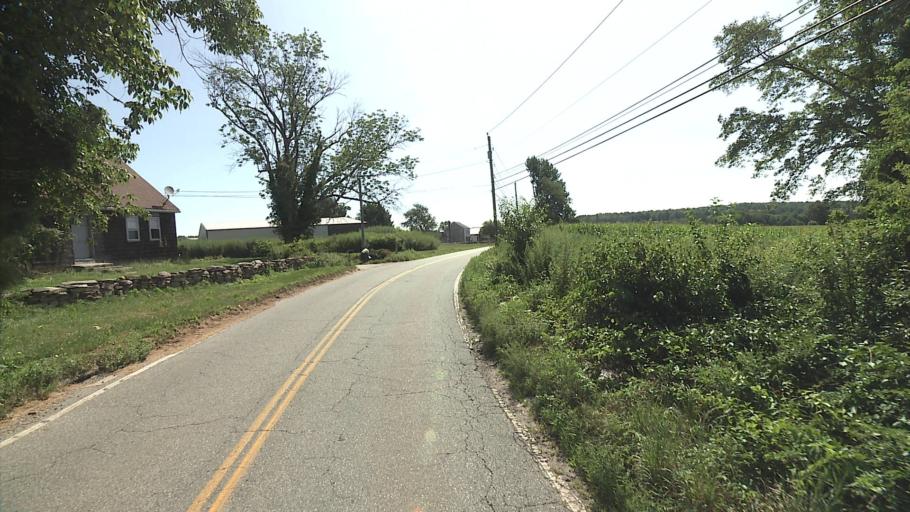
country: US
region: Connecticut
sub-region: Windham County
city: South Windham
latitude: 41.6387
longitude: -72.1734
